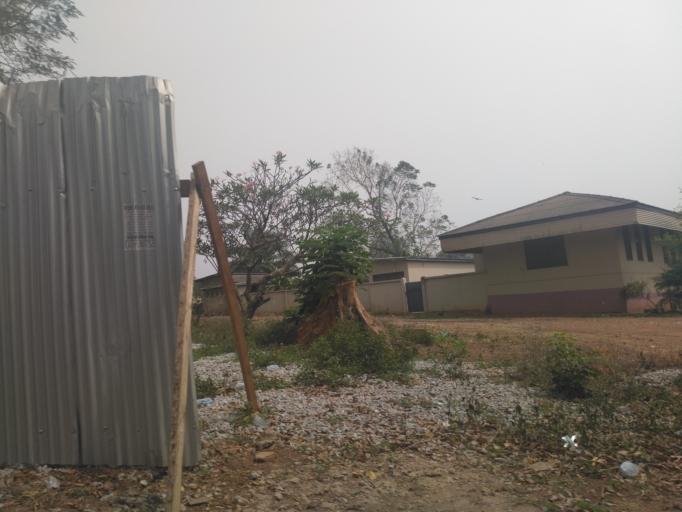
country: GH
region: Ashanti
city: Kumasi
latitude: 6.6911
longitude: -1.6340
